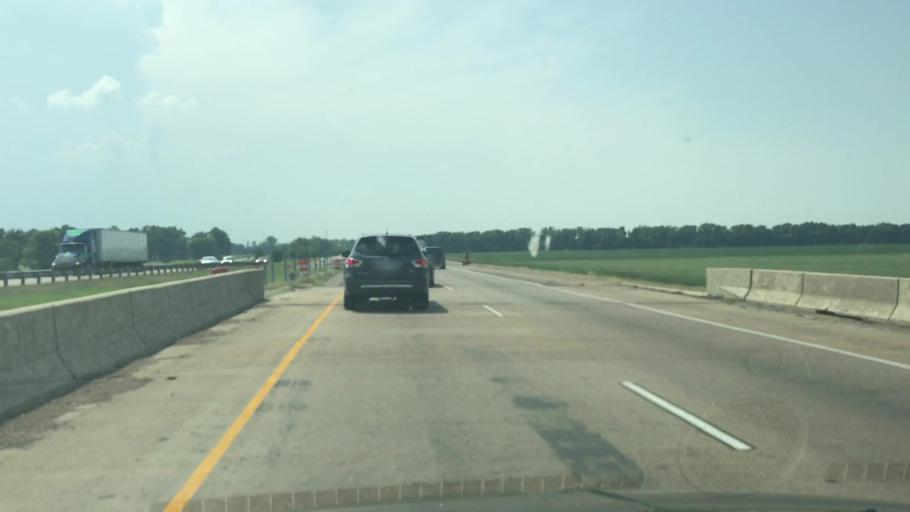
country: US
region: Arkansas
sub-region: Crittenden County
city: West Memphis
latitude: 35.1483
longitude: -90.3283
